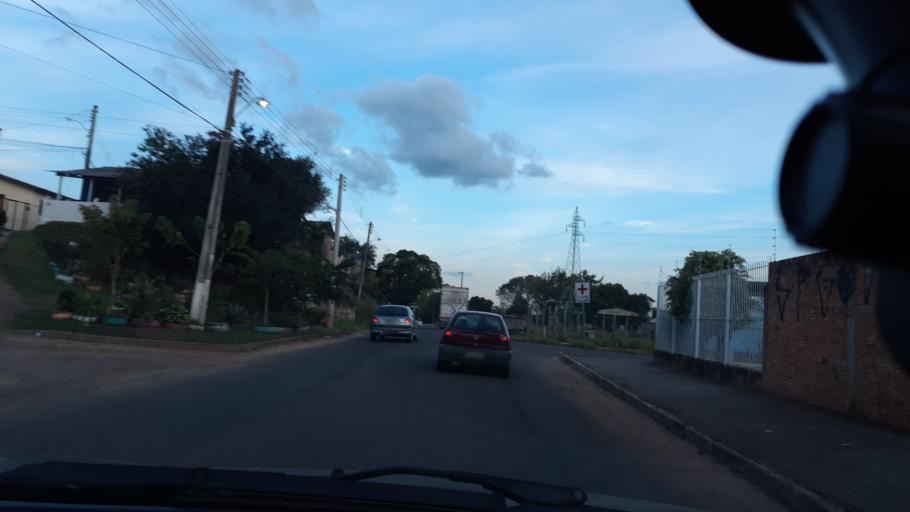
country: BR
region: Rio Grande do Sul
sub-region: Sapucaia Do Sul
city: Sapucaia
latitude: -29.8405
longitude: -51.1546
